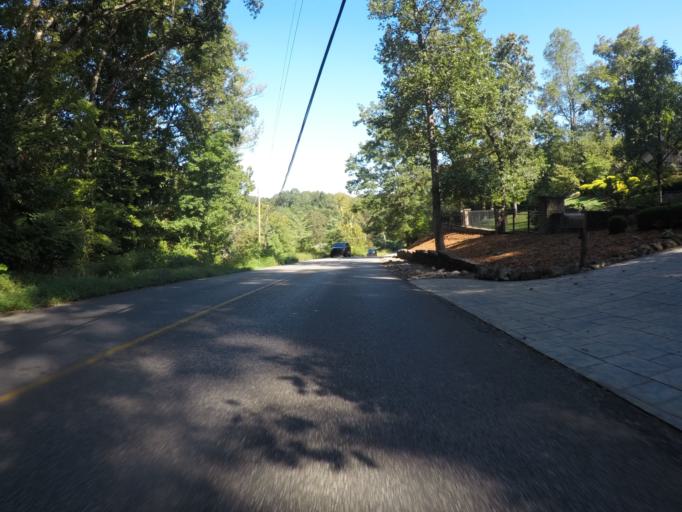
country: US
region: Kentucky
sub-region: Greenup County
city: Russell
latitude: 38.4971
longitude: -82.6963
